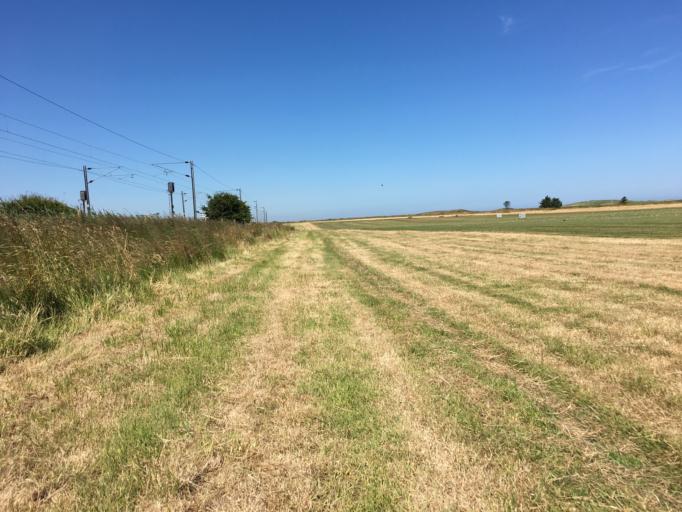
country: GB
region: England
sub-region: Northumberland
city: Ancroft
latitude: 55.7071
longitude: -1.9291
